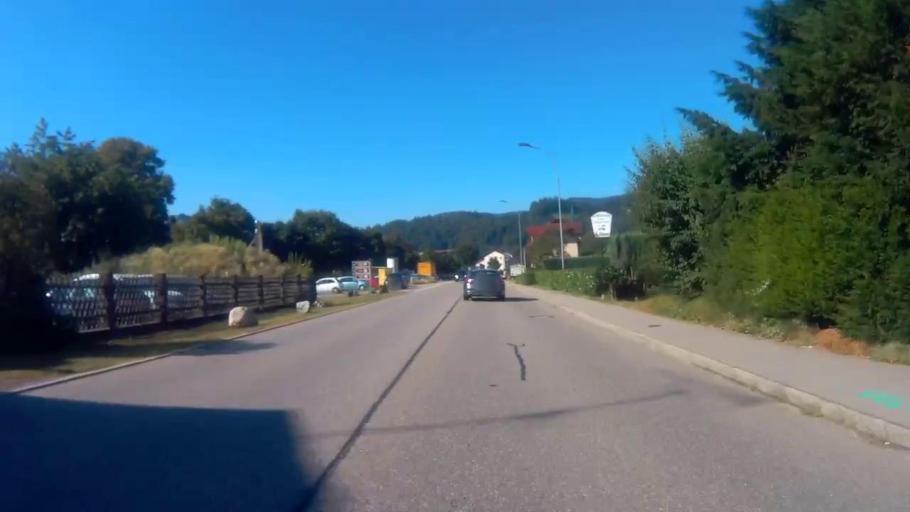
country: DE
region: Baden-Wuerttemberg
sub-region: Freiburg Region
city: Schonau im Schwarzwald
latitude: 47.7913
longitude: 7.9000
